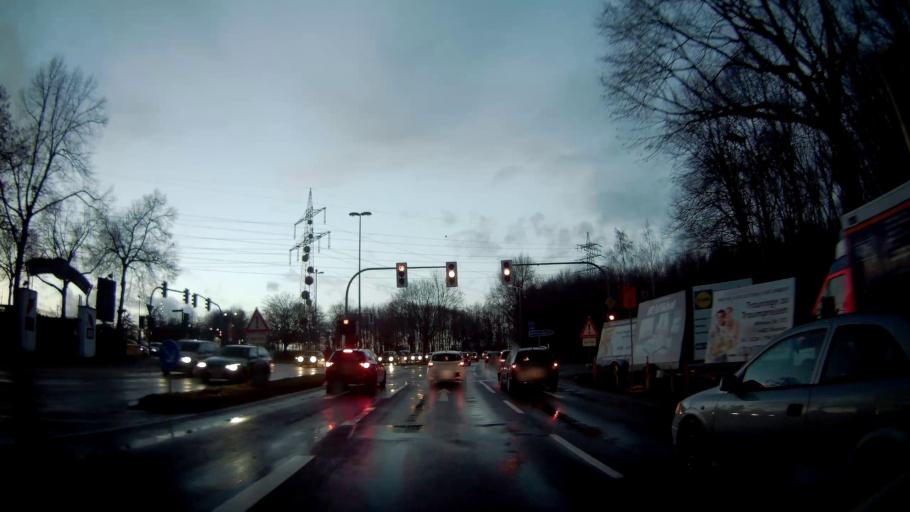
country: DE
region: North Rhine-Westphalia
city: Castrop-Rauxel
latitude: 51.4943
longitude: 7.2901
